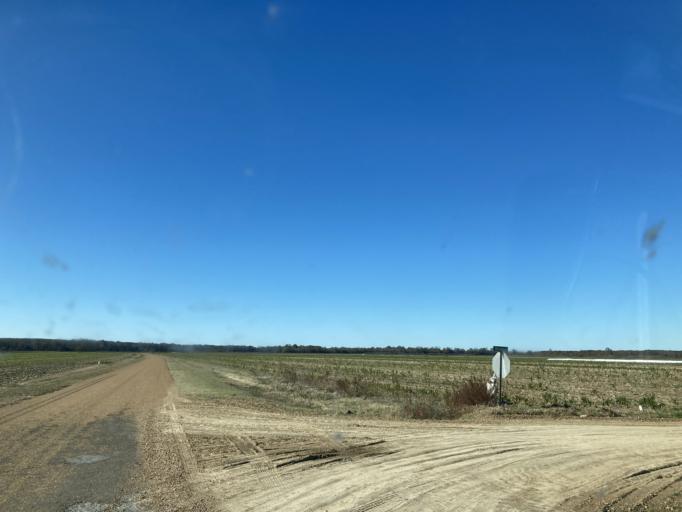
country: US
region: Mississippi
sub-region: Hinds County
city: Lynchburg
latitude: 32.6257
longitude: -90.5754
